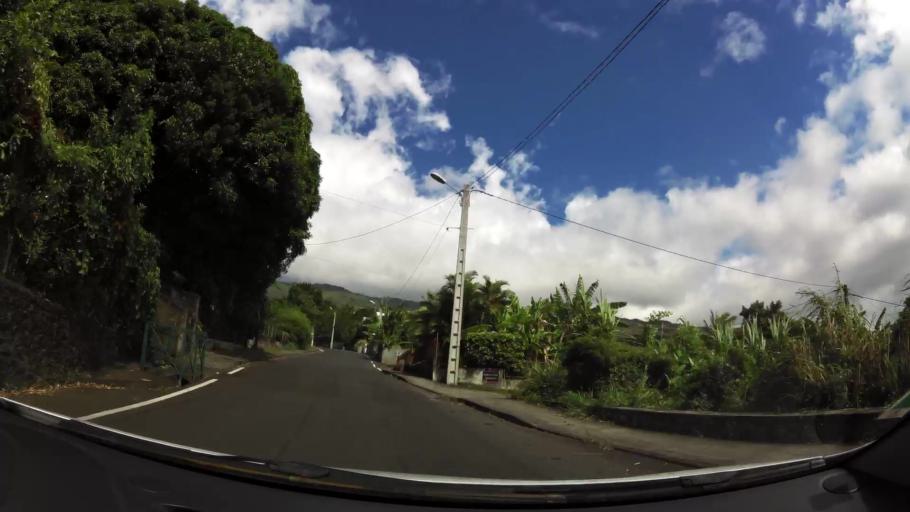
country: RE
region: Reunion
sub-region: Reunion
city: Saint-Denis
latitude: -20.9300
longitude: 55.4934
